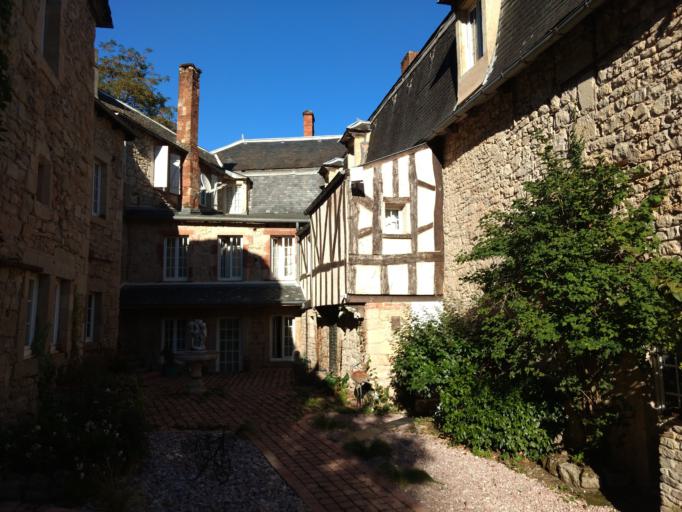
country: FR
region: Midi-Pyrenees
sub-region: Departement de l'Aveyron
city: Valady
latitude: 44.4464
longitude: 2.4485
